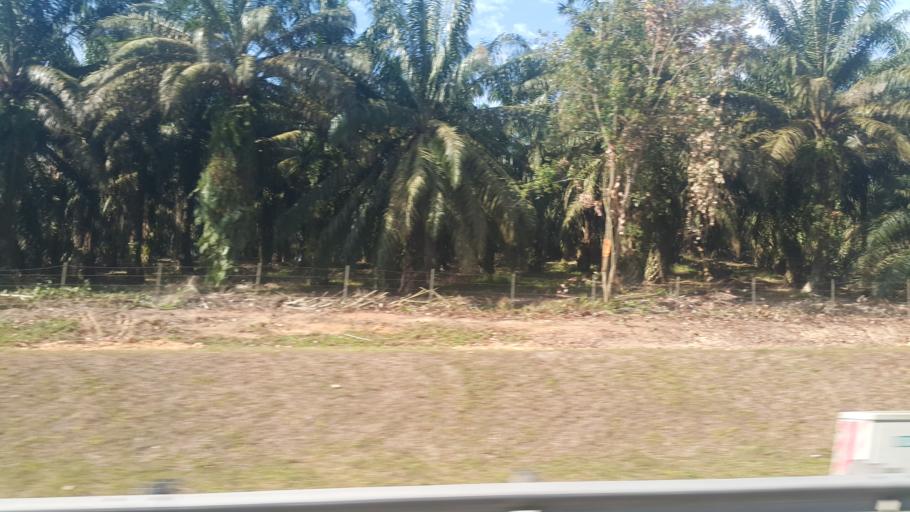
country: MY
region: Johor
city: Kelapa Sawit
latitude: 1.7268
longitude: 103.4265
